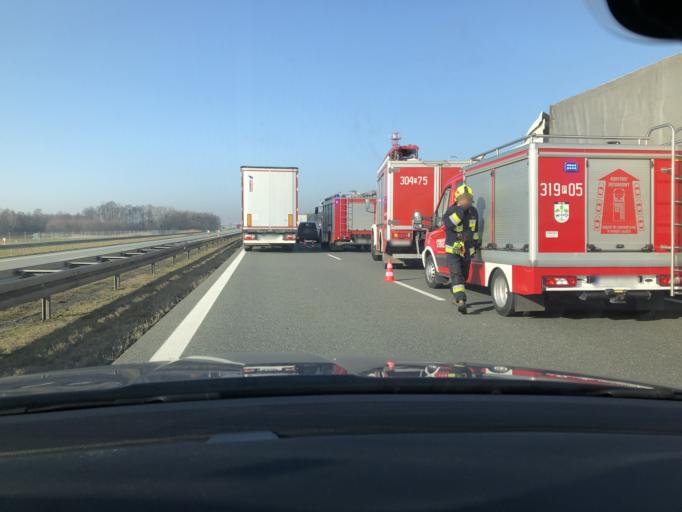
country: PL
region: Greater Poland Voivodeship
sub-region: Powiat poznanski
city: Buk
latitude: 52.3720
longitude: 16.5804
